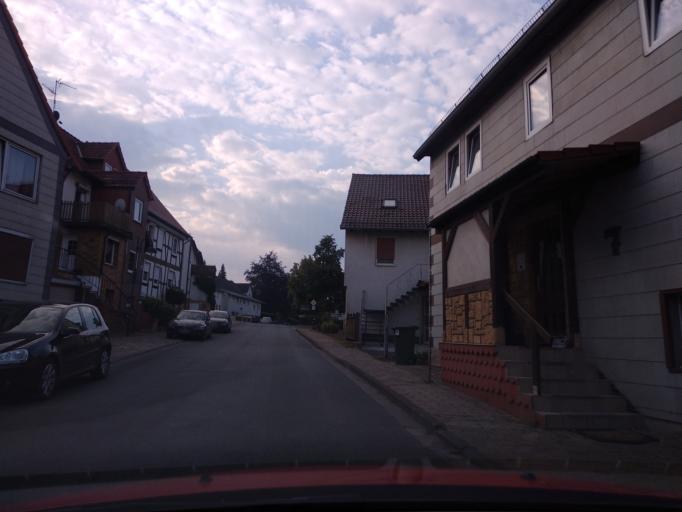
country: DE
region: Hesse
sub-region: Regierungsbezirk Kassel
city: Calden
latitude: 51.3835
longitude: 9.3653
